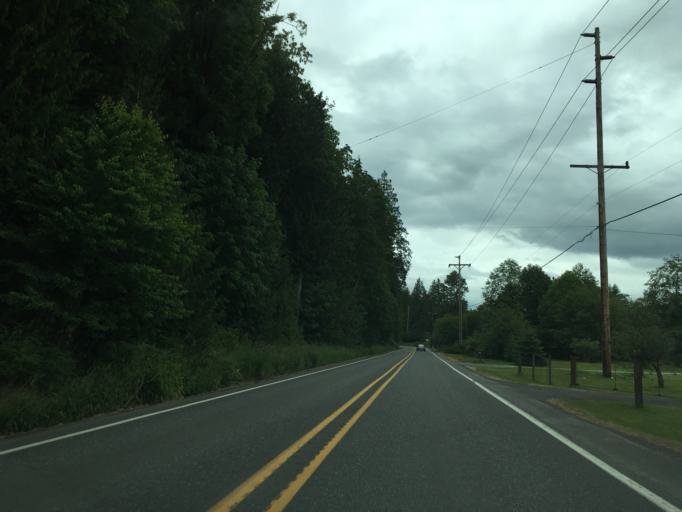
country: US
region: Washington
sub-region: Whatcom County
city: Peaceful Valley
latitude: 48.8637
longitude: -122.1530
